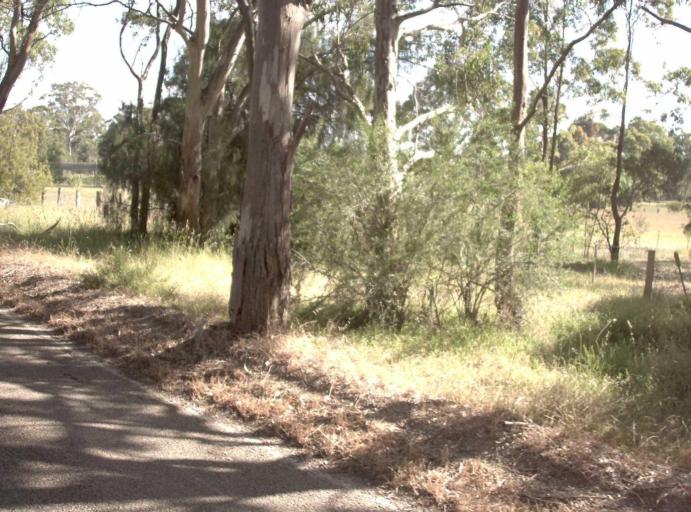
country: AU
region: Victoria
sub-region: East Gippsland
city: Lakes Entrance
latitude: -37.7938
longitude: 147.8313
